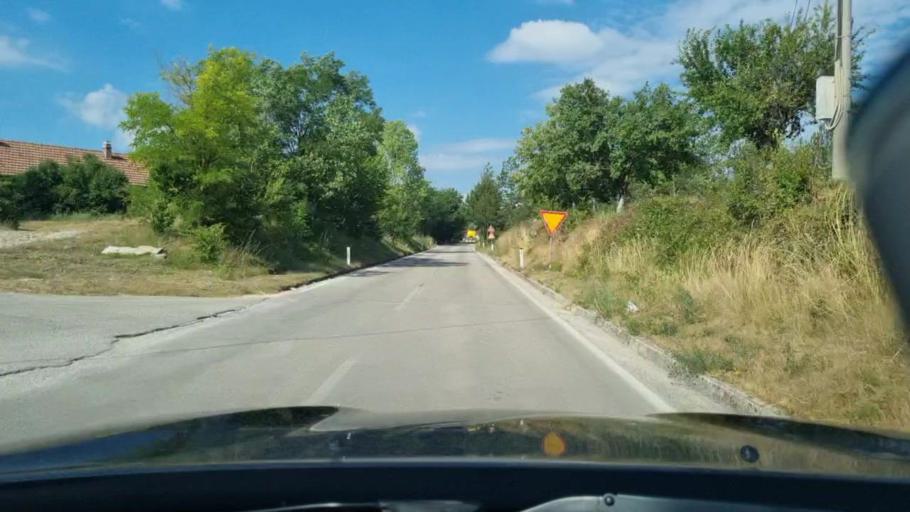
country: BA
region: Federation of Bosnia and Herzegovina
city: Dreznica
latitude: 43.4644
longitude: 17.3005
